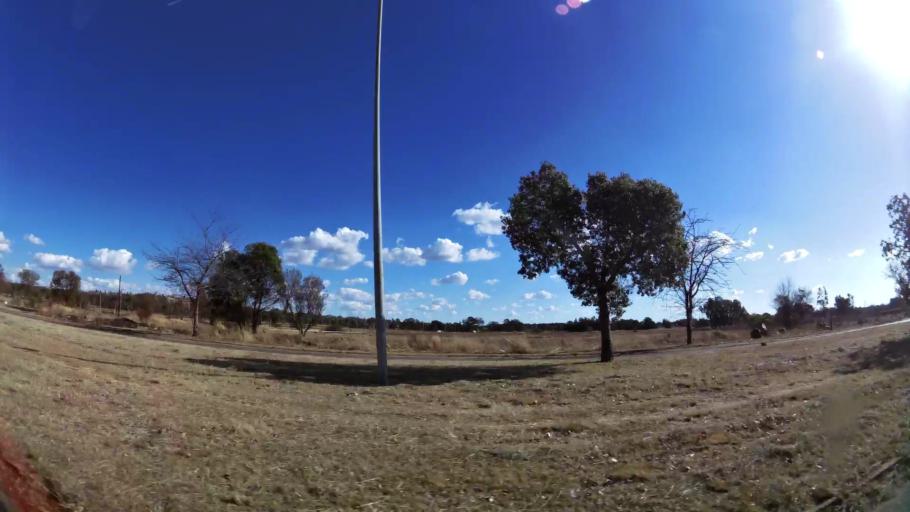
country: ZA
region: Gauteng
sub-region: West Rand District Municipality
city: Carletonville
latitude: -26.3721
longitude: 27.3966
